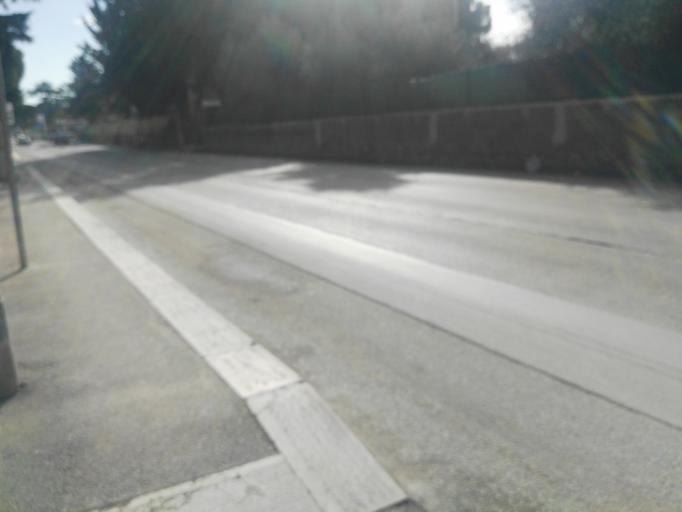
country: IT
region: Apulia
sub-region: Provincia di Barletta - Andria - Trani
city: Andria
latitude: 41.2183
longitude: 16.3078
